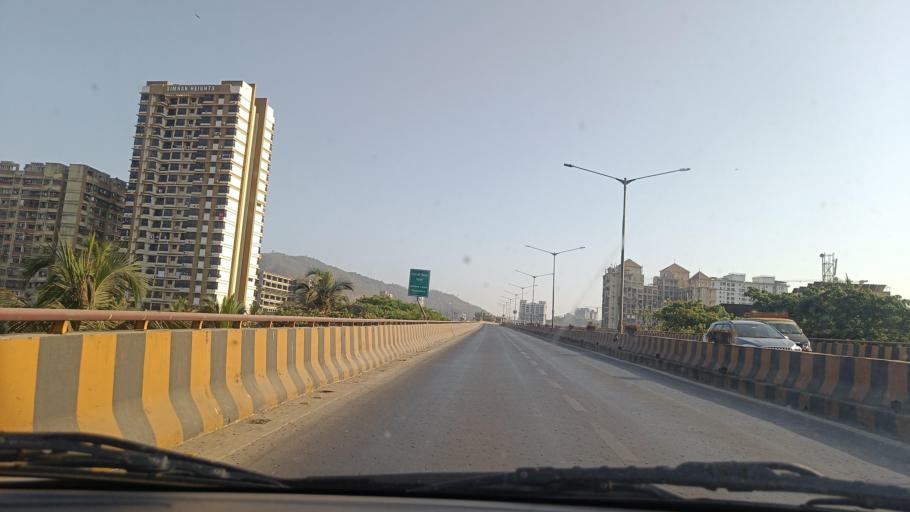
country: IN
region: Maharashtra
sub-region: Mumbai Suburban
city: Mumbai
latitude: 19.0529
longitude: 72.9107
